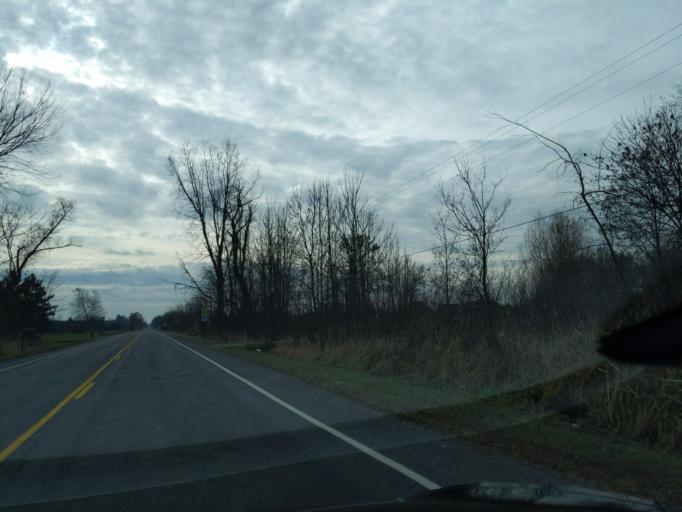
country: US
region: Michigan
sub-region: Ingham County
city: Holt
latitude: 42.5895
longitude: -84.5230
